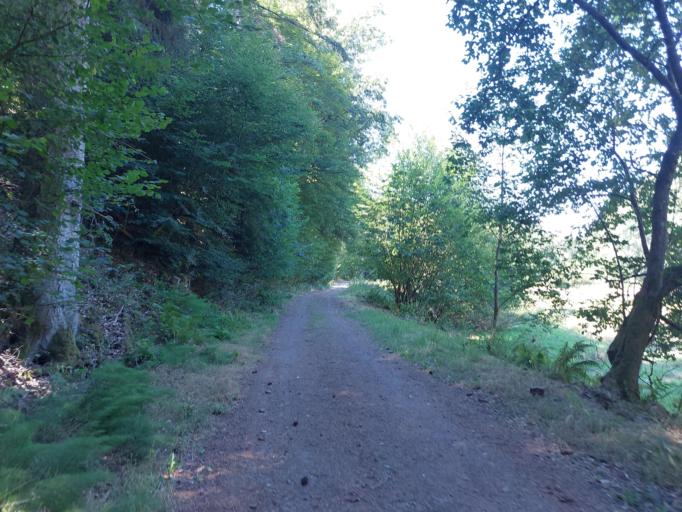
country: DE
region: Rheinland-Pfalz
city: Grosslittgen
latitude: 50.0226
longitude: 6.7621
